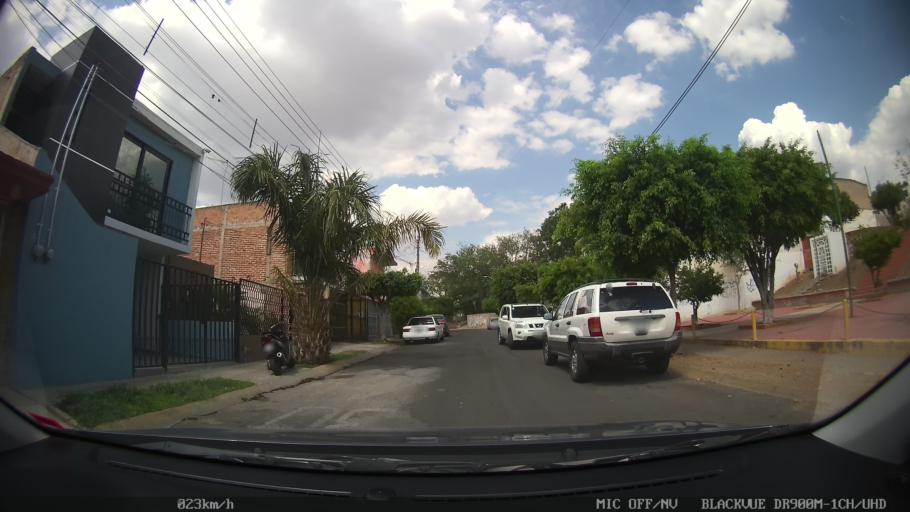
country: MX
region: Jalisco
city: Tlaquepaque
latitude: 20.6288
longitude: -103.2651
